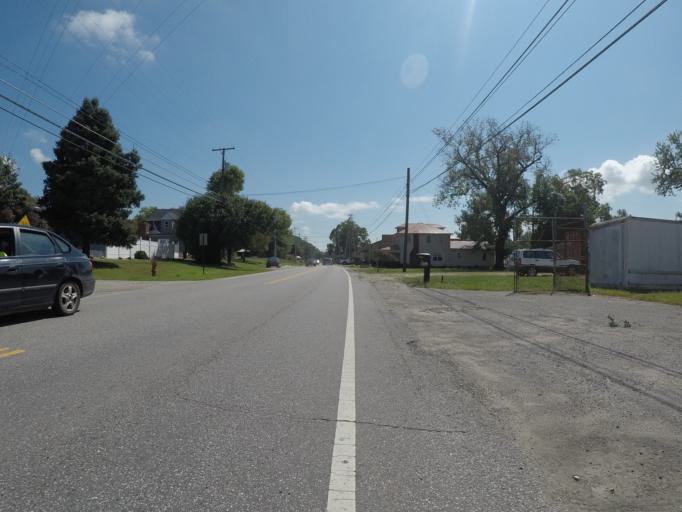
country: US
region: Ohio
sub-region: Lawrence County
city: South Point
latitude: 38.4127
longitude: -82.5799
